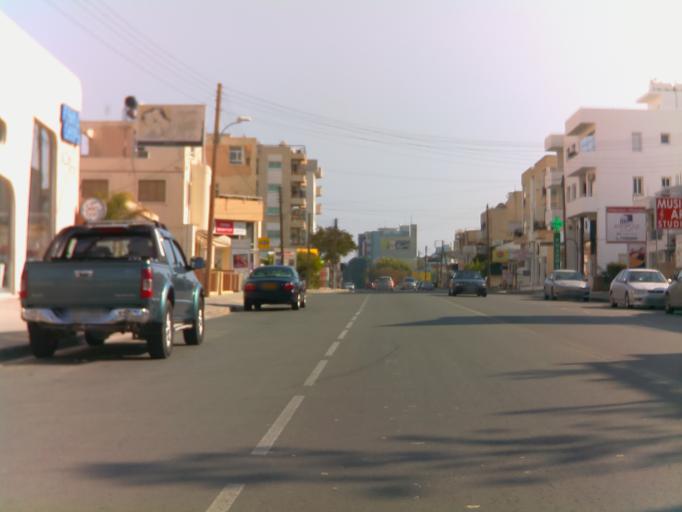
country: CY
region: Larnaka
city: Larnaca
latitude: 34.9111
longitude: 33.6205
